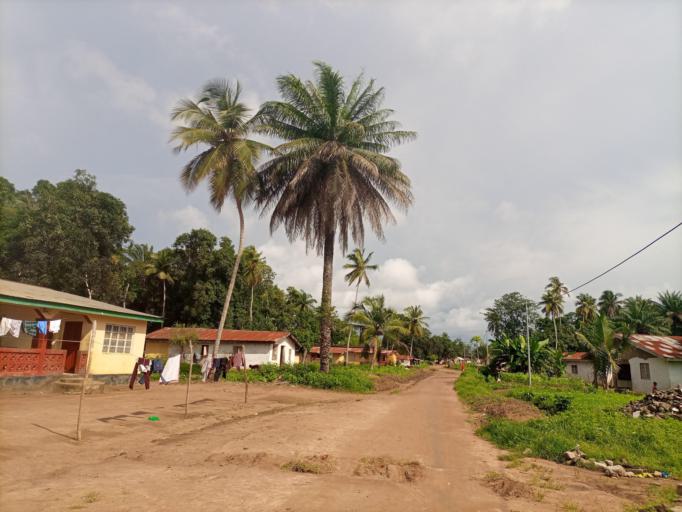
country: SL
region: Northern Province
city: Masoyila
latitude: 8.6154
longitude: -13.1714
